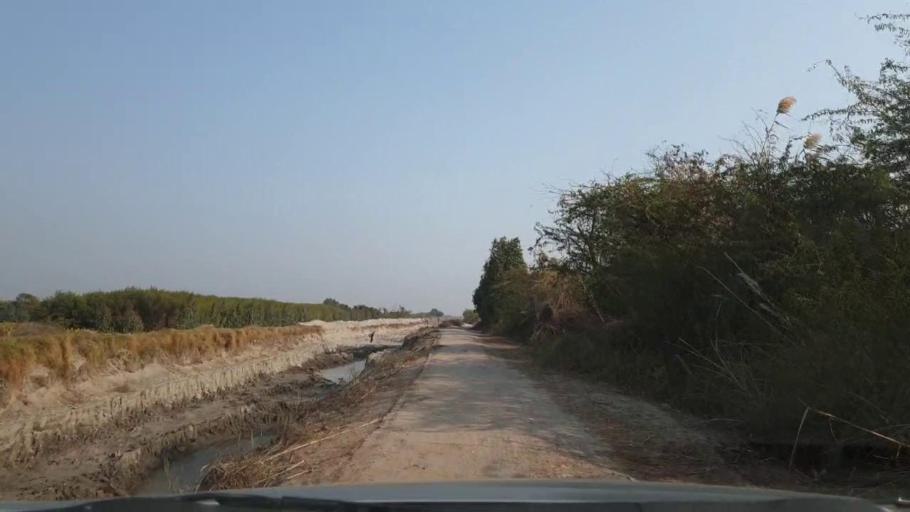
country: PK
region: Sindh
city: Tando Adam
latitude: 25.6492
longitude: 68.5938
